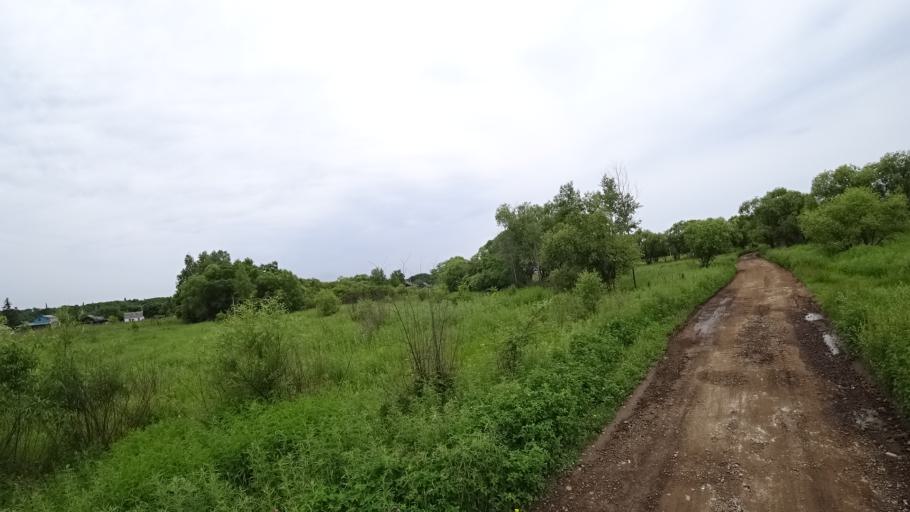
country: RU
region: Primorskiy
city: Novosysoyevka
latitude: 44.2077
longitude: 133.3289
